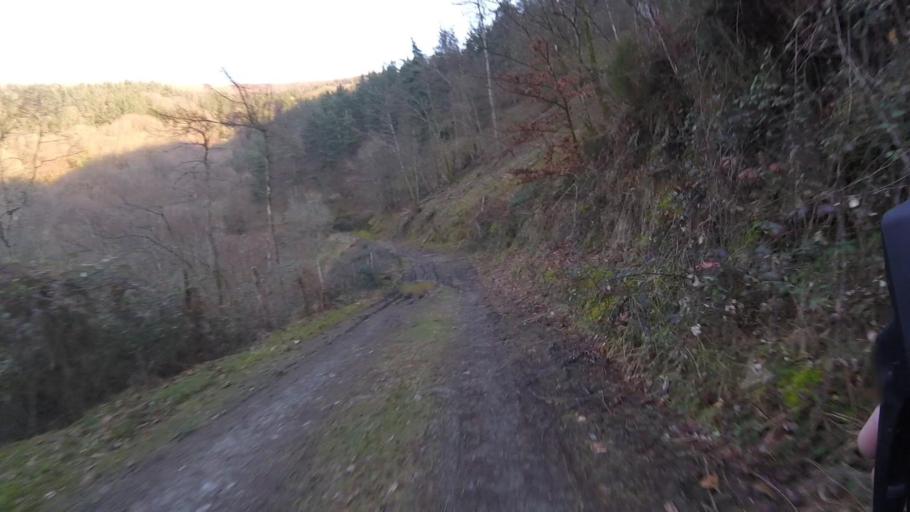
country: ES
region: Navarre
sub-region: Provincia de Navarra
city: Arano
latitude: 43.2467
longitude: -1.8586
